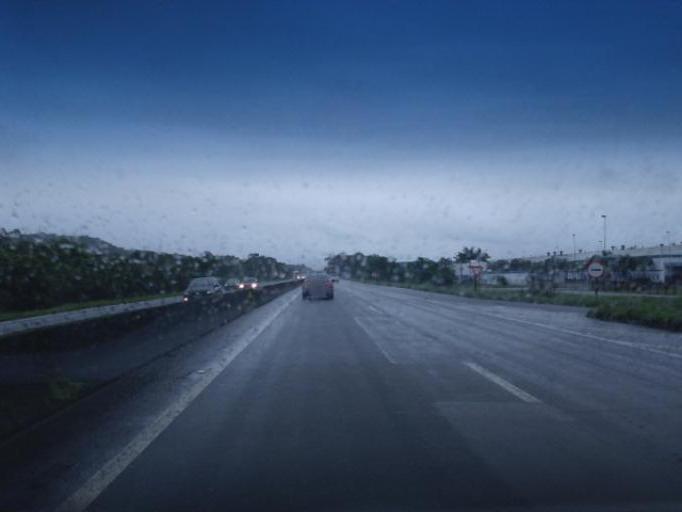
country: BR
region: Santa Catarina
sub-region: Joinville
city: Joinville
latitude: -26.0793
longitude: -48.8615
